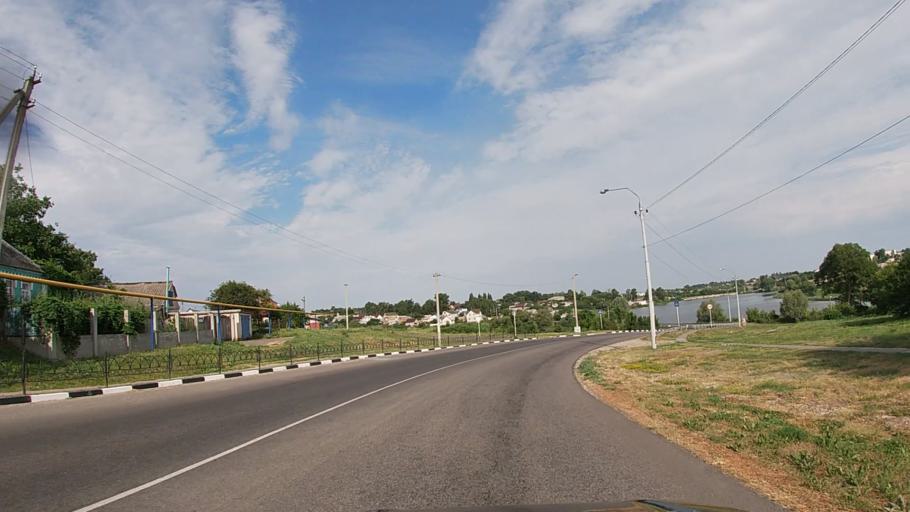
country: RU
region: Belgorod
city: Krasnaya Yaruga
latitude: 50.8001
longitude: 35.6726
